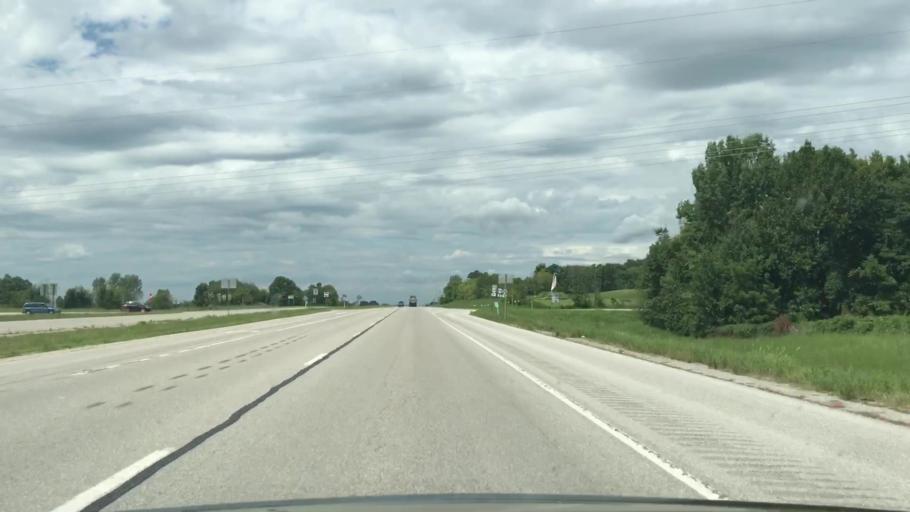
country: US
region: Kentucky
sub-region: Todd County
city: Elkton
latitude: 36.8227
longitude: -87.1981
